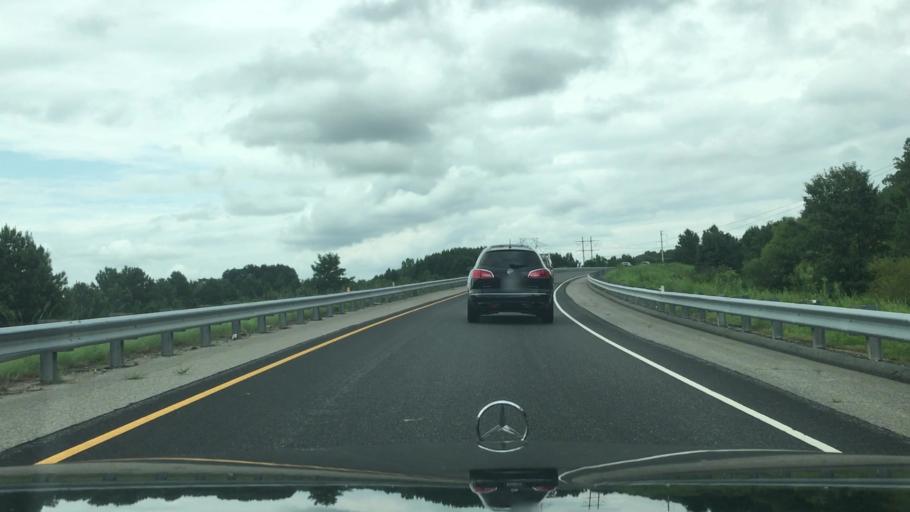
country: US
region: Virginia
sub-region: Chesterfield County
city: Brandermill
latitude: 37.4575
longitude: -77.6373
